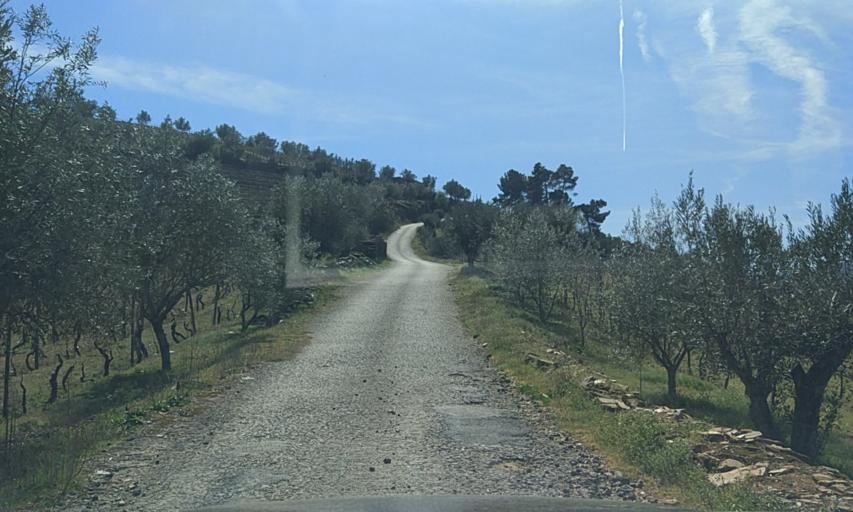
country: PT
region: Vila Real
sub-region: Sabrosa
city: Sabrosa
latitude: 41.3050
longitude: -7.5461
